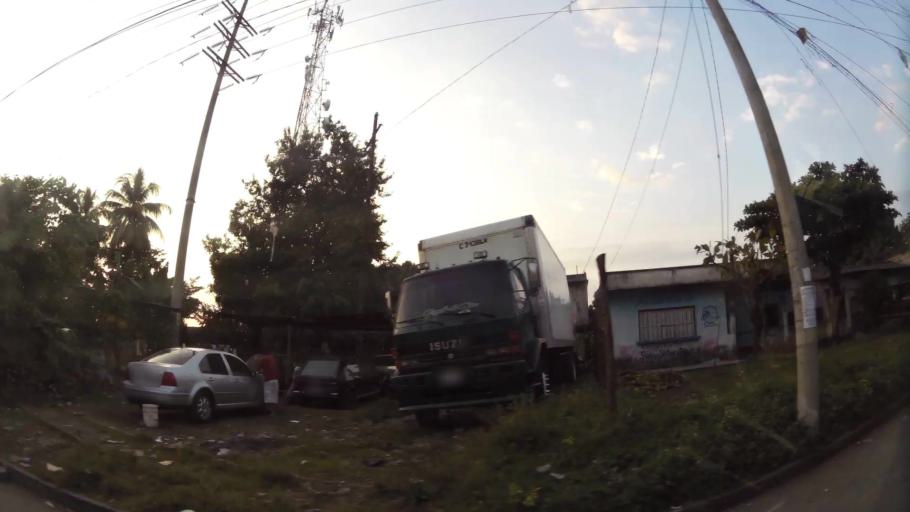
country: GT
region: Retalhuleu
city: San Sebastian
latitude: 14.5648
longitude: -91.6511
